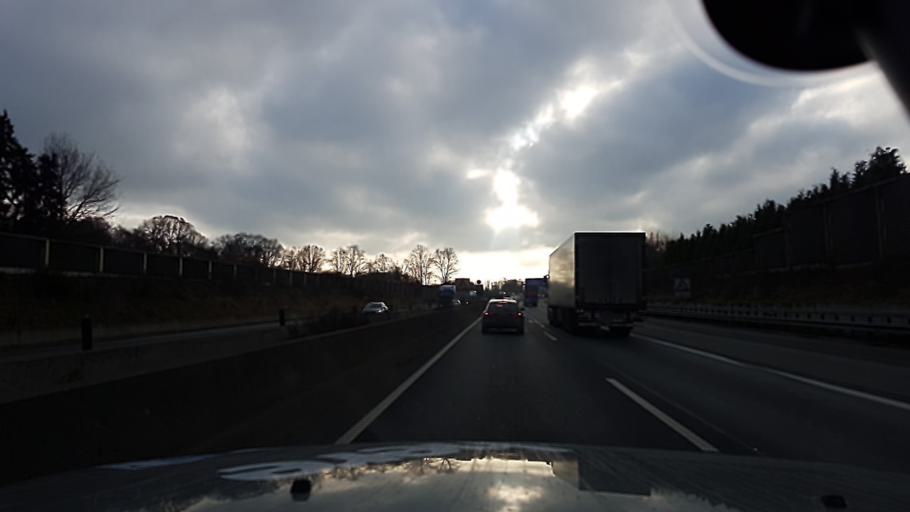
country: DE
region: North Rhine-Westphalia
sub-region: Regierungsbezirk Munster
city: Lotte
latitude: 52.2865
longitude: 7.9391
